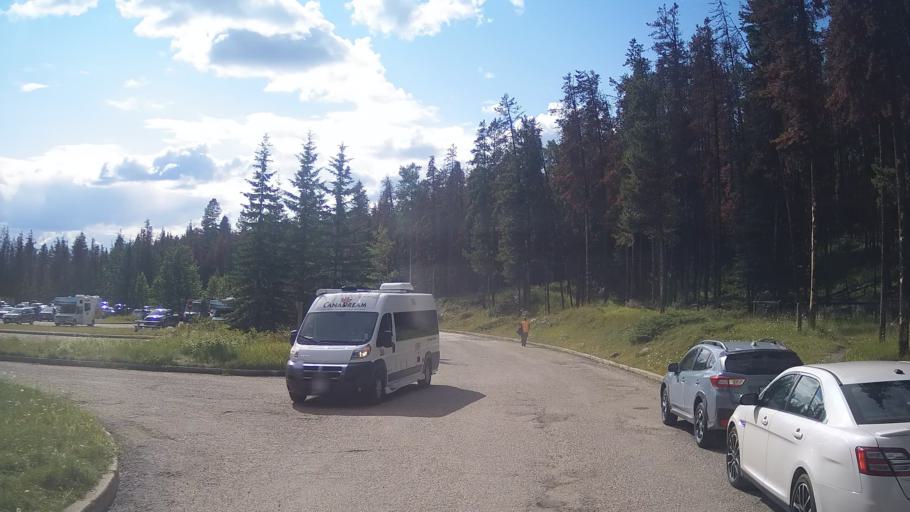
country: CA
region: Alberta
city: Jasper Park Lodge
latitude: 52.9211
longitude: -117.9982
